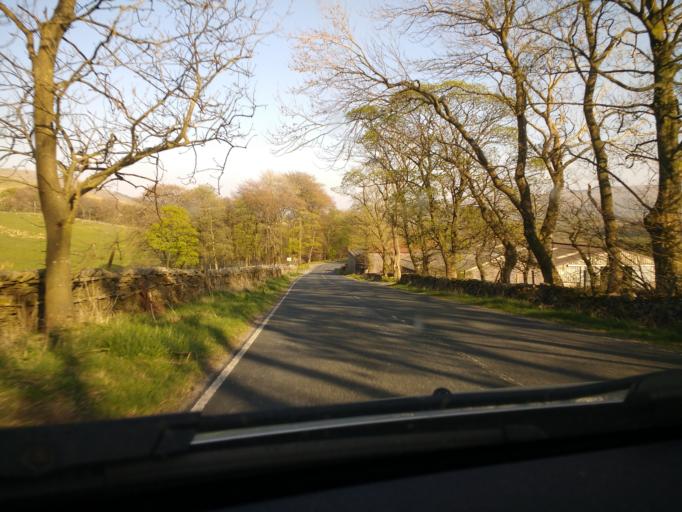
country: GB
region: England
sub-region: Cumbria
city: Kirkby Stephen
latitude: 54.3246
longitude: -2.2459
